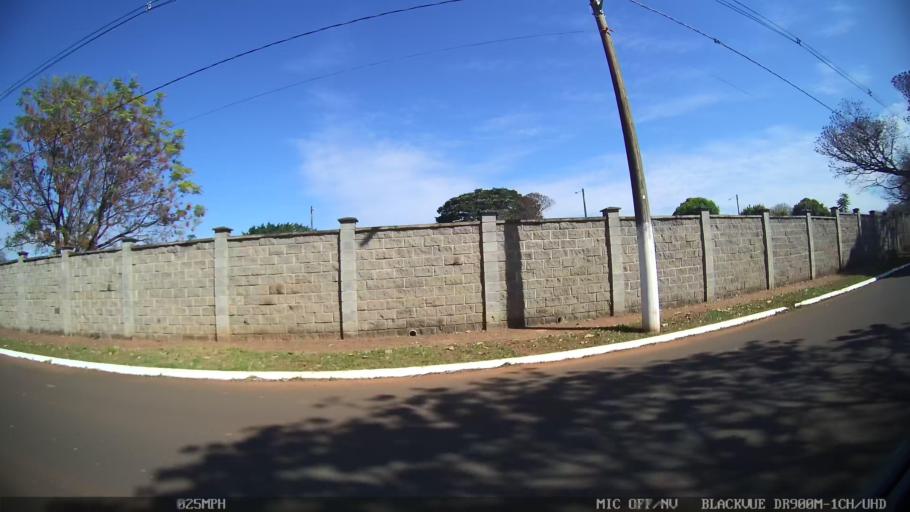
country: BR
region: Sao Paulo
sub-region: Santa Barbara D'Oeste
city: Santa Barbara d'Oeste
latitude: -22.7397
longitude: -47.4140
